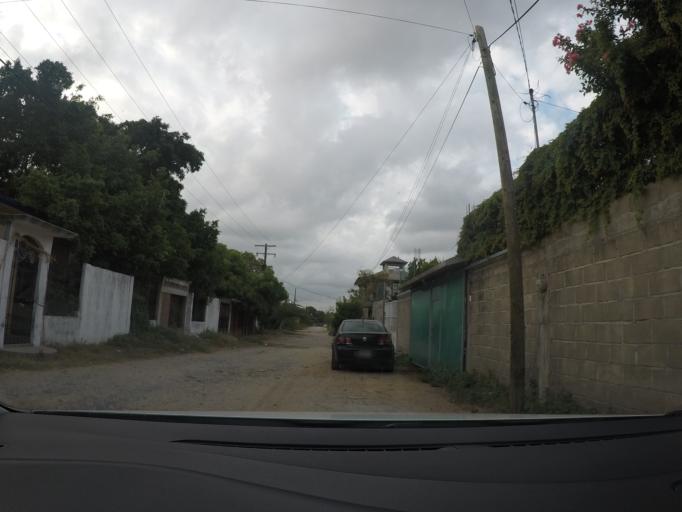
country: MX
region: Oaxaca
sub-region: Salina Cruz
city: Salina Cruz
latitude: 16.2108
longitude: -95.1975
